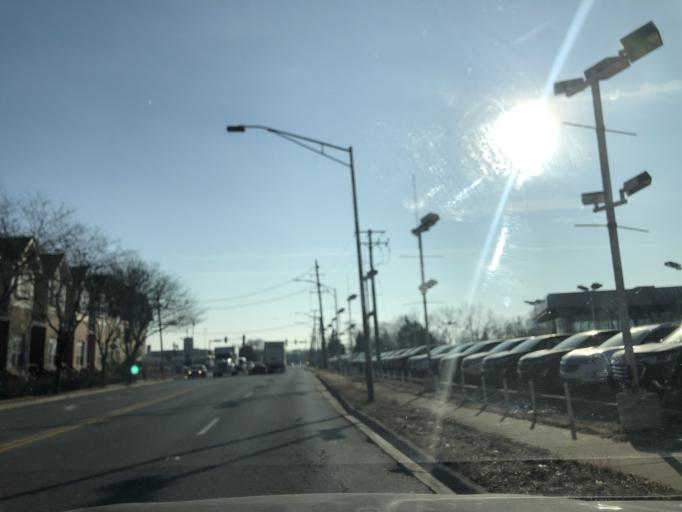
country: US
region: Illinois
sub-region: Cook County
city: Forest Park
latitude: 41.8661
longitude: -87.8189
